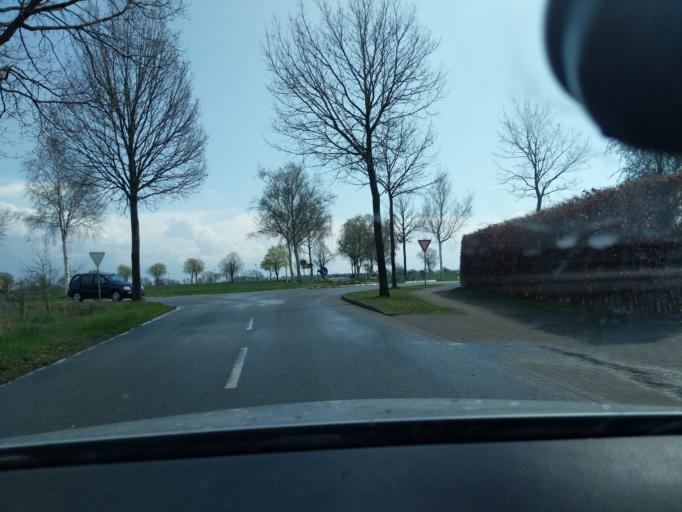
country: DE
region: Lower Saxony
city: Ahlerstedt
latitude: 53.4026
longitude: 9.4640
